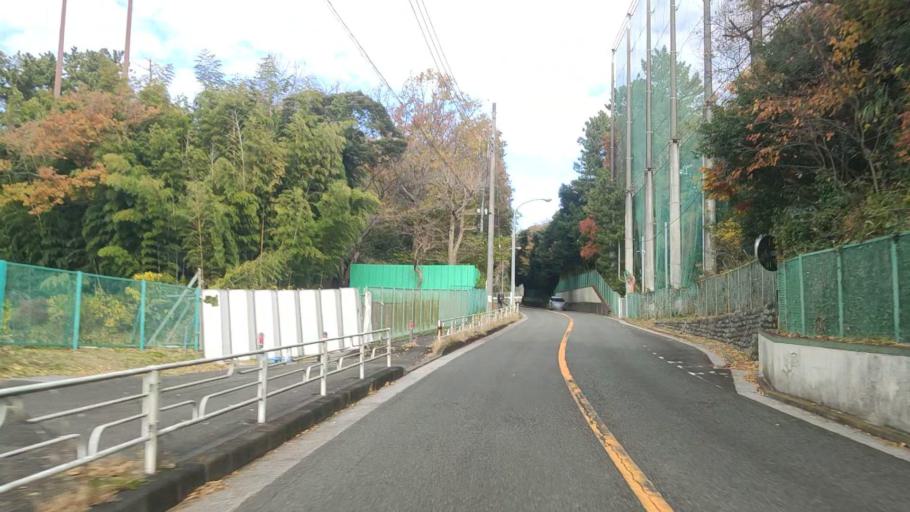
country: JP
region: Kanagawa
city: Yokohama
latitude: 35.4424
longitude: 139.5441
